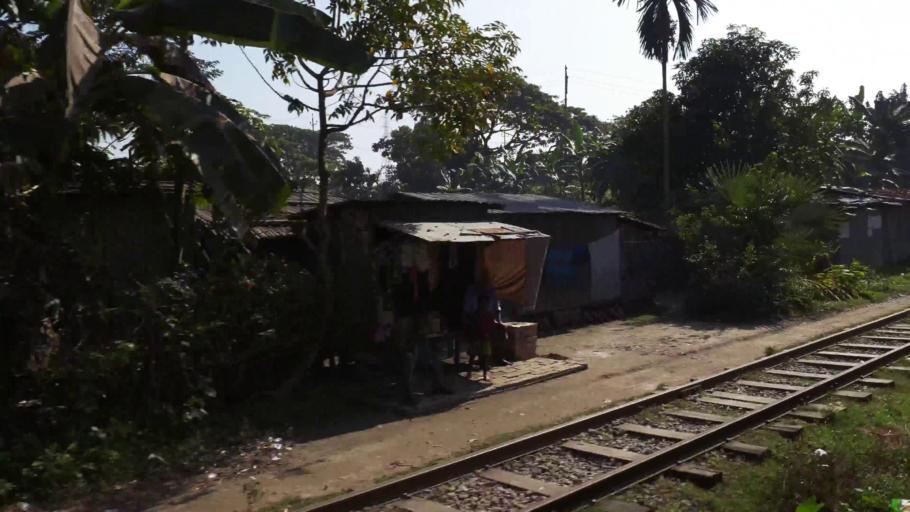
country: BD
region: Dhaka
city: Mymensingh
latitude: 24.6114
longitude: 90.4834
